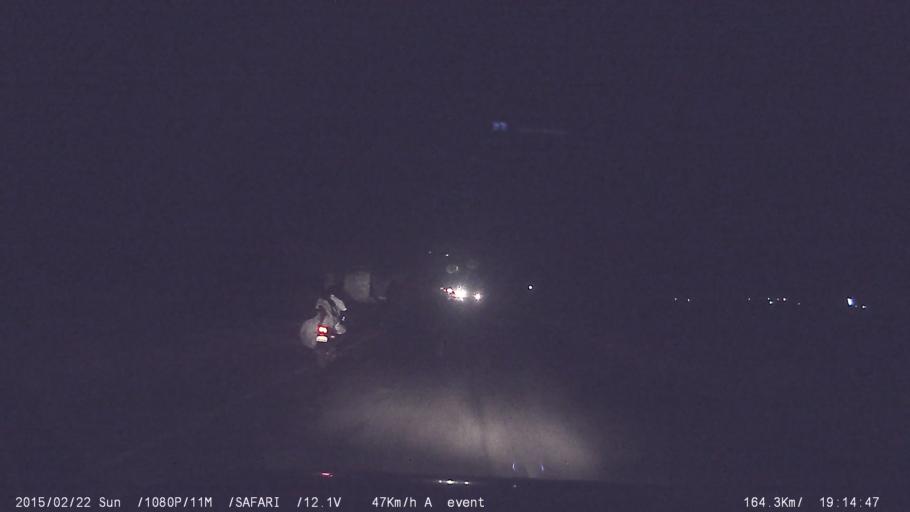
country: IN
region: Tamil Nadu
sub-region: Theni
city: Periyakulam
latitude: 10.0859
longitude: 77.5232
